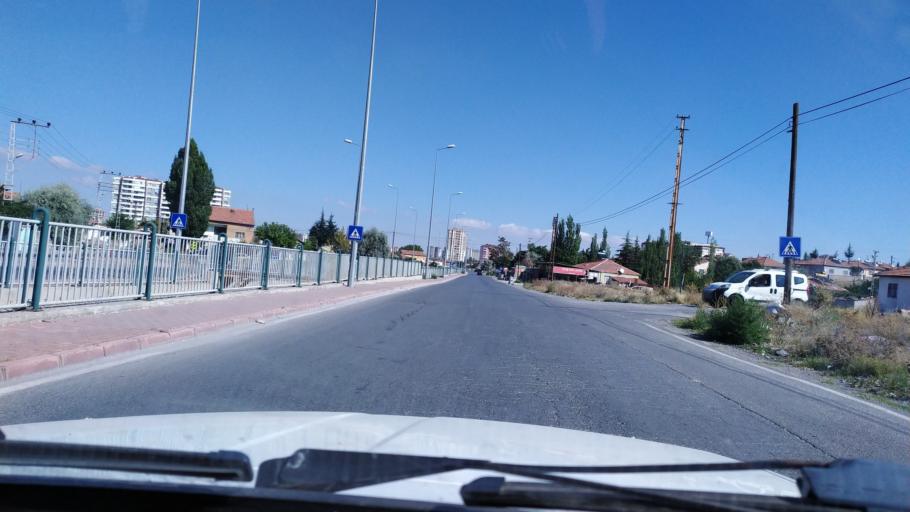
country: TR
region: Kayseri
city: Talas
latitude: 38.7215
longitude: 35.5503
